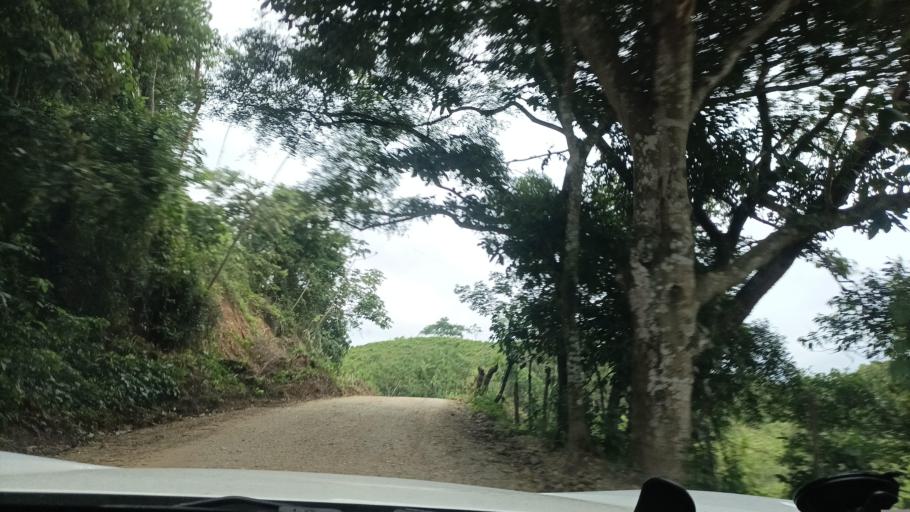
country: MX
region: Veracruz
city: Hidalgotitlan
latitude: 17.6186
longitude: -94.5155
